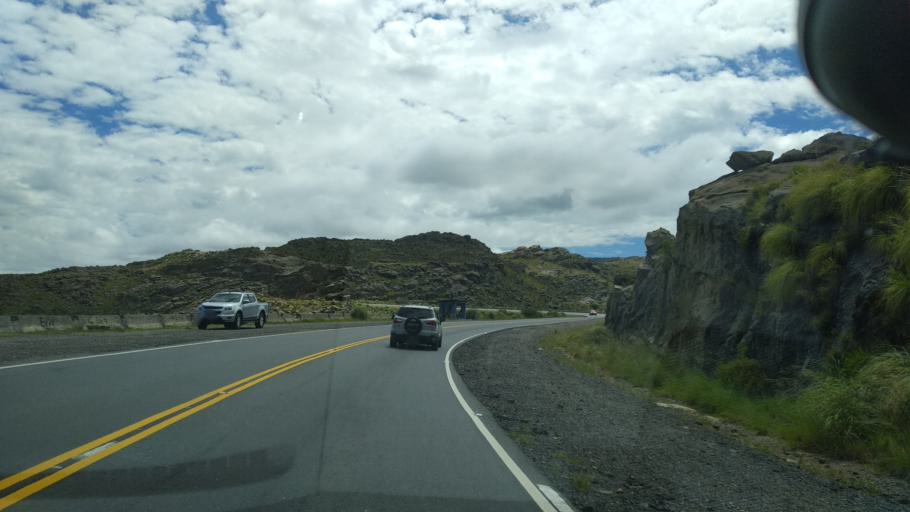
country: AR
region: Cordoba
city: Mina Clavero
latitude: -31.7499
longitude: -64.9111
